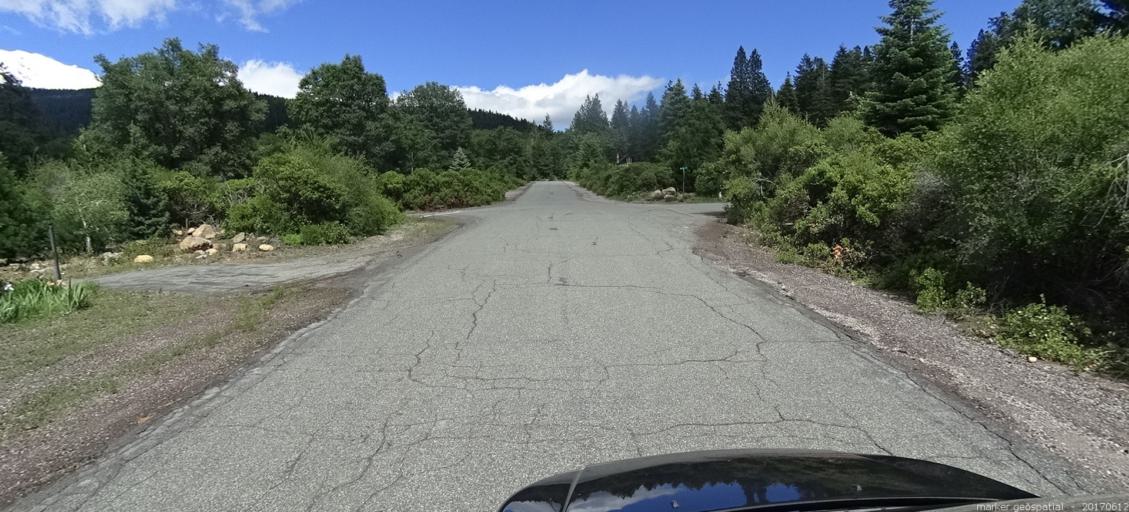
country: US
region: California
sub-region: Siskiyou County
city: Mount Shasta
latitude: 41.3156
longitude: -122.2846
